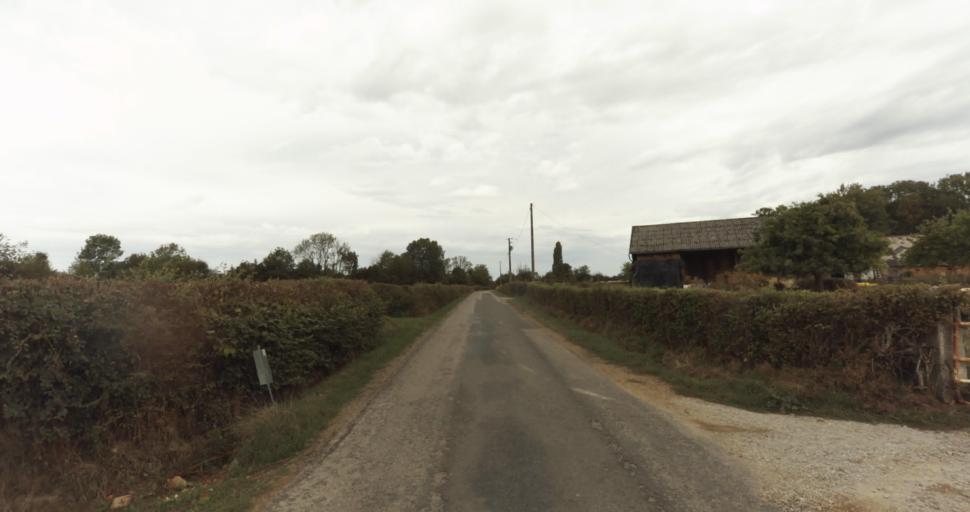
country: FR
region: Lower Normandy
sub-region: Departement de l'Orne
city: Vimoutiers
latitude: 48.9178
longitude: 0.2999
